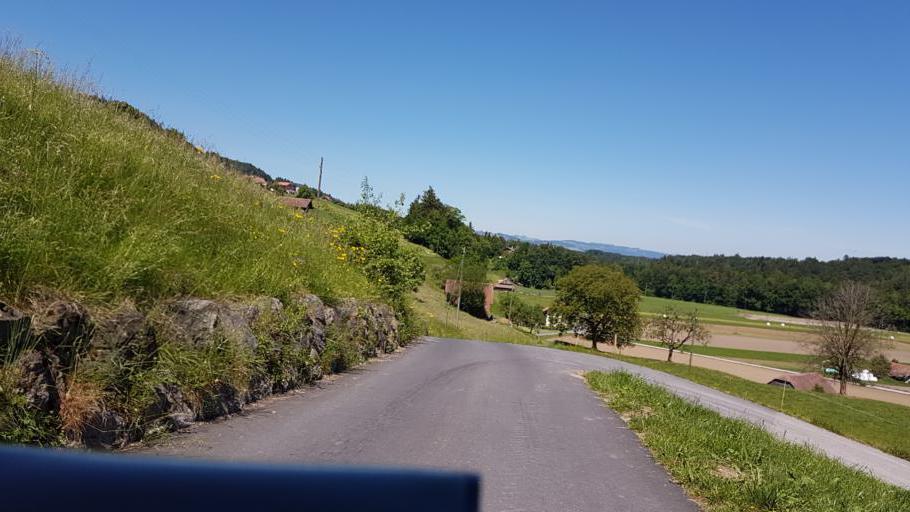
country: CH
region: Bern
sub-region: Frutigen-Niedersimmental District
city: Wimmis
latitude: 46.7075
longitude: 7.6244
